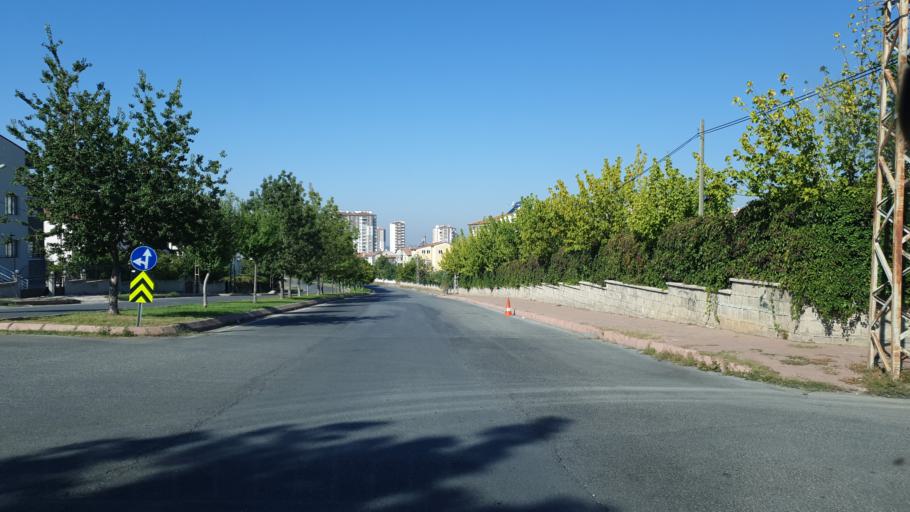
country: TR
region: Kayseri
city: Kocasinan
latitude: 38.7774
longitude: 35.5855
